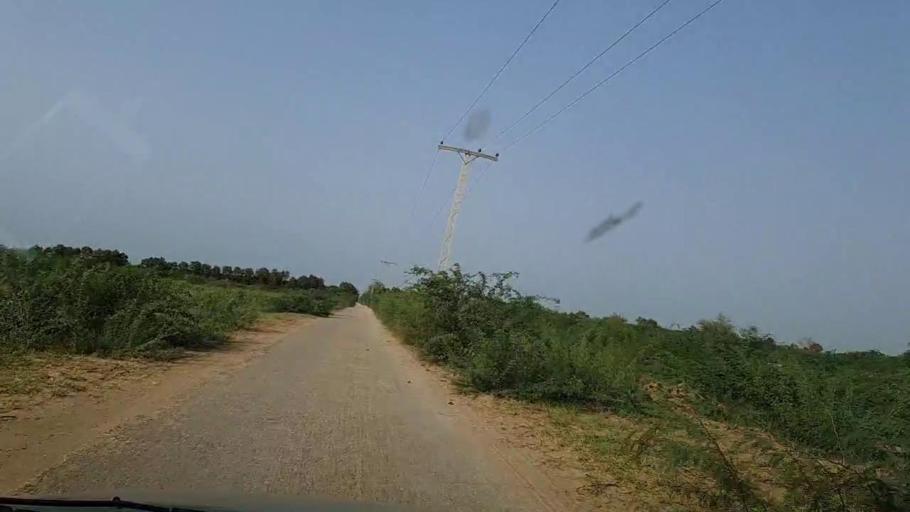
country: PK
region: Sindh
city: Kotri
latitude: 25.2222
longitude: 68.2479
